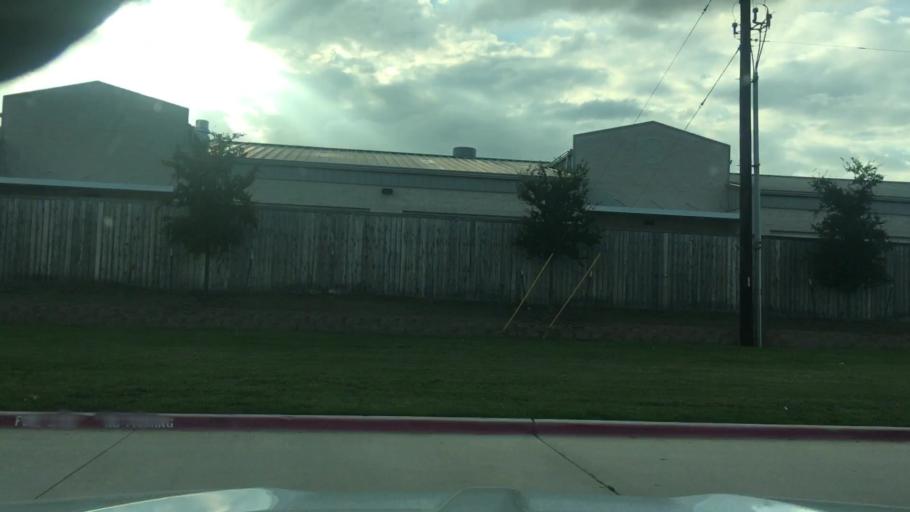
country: US
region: Texas
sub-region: Denton County
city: Cross Roads
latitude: 33.2240
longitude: -96.9830
